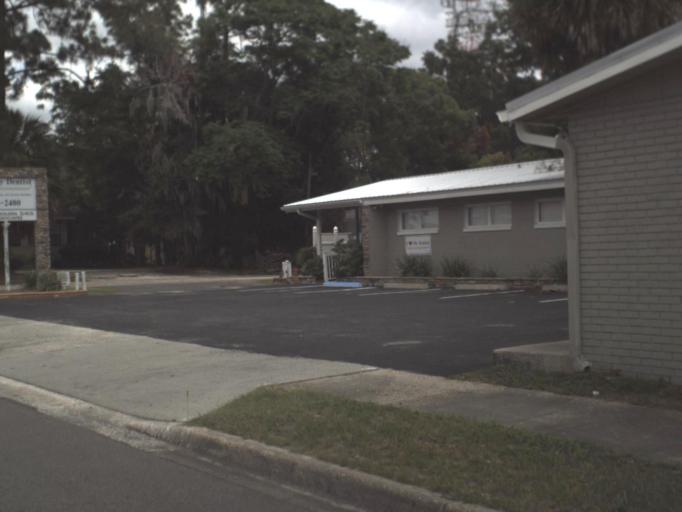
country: US
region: Florida
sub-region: Columbia County
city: Lake City
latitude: 30.1870
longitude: -82.6393
